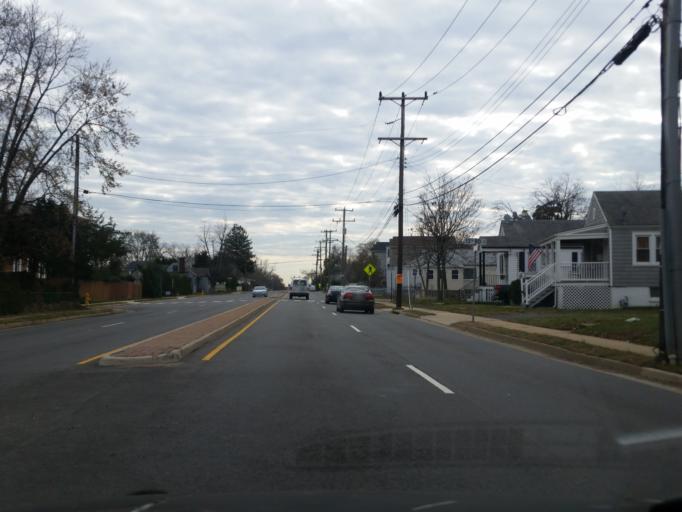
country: US
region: Virginia
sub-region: Arlington County
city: Arlington
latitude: 38.8583
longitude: -77.0909
